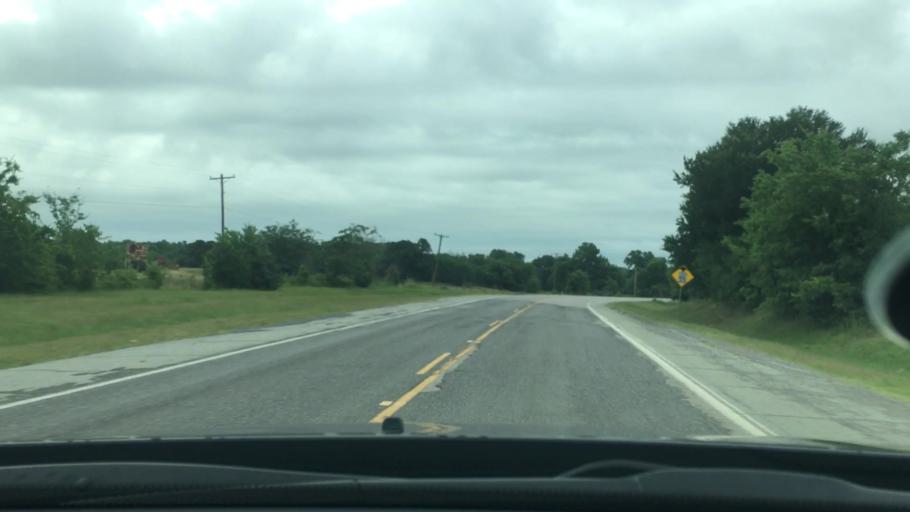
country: US
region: Oklahoma
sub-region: Coal County
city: Coalgate
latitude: 34.5492
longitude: -96.2321
